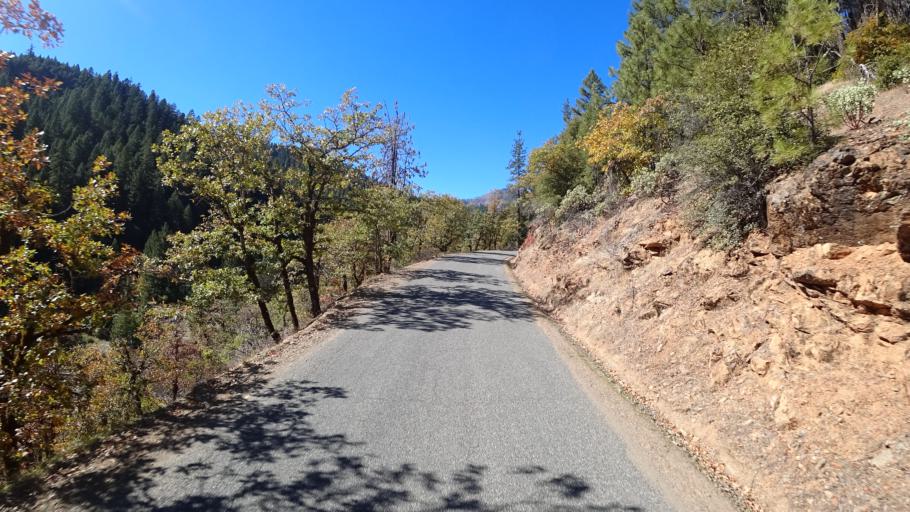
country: US
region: California
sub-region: Siskiyou County
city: Happy Camp
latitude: 41.3028
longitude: -123.1609
